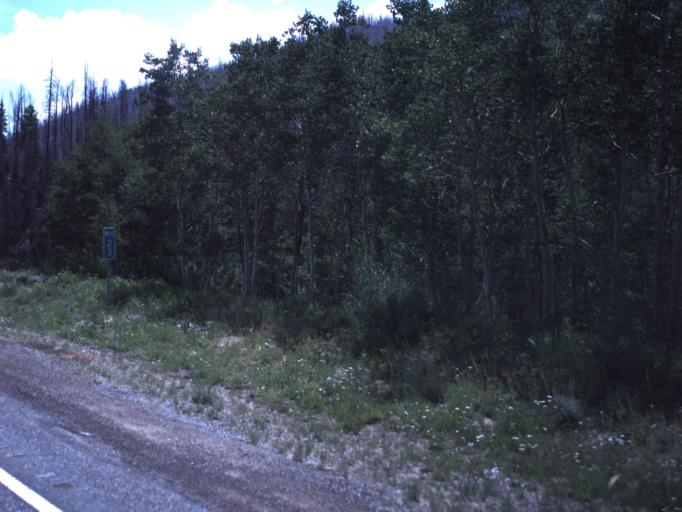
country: US
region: Utah
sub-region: Sanpete County
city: Fairview
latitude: 39.5910
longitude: -111.1962
